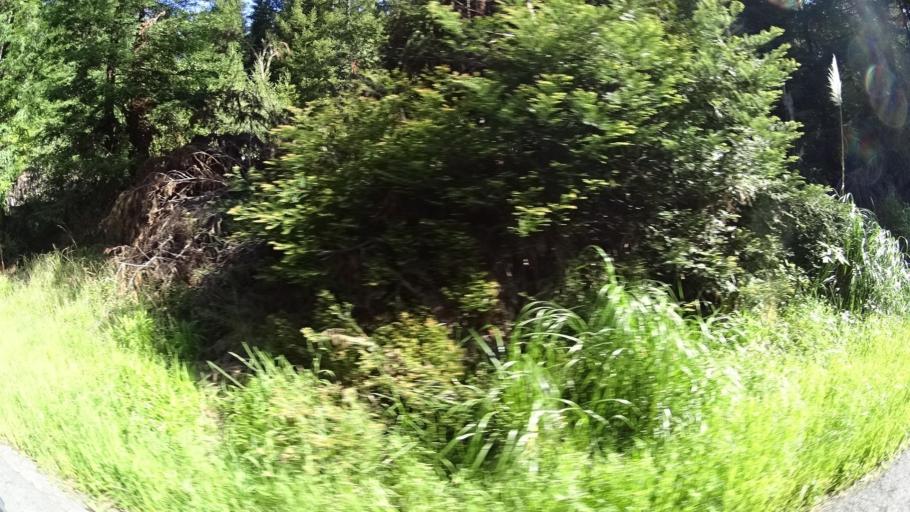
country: US
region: California
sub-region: Humboldt County
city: Rio Dell
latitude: 40.4568
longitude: -124.0348
